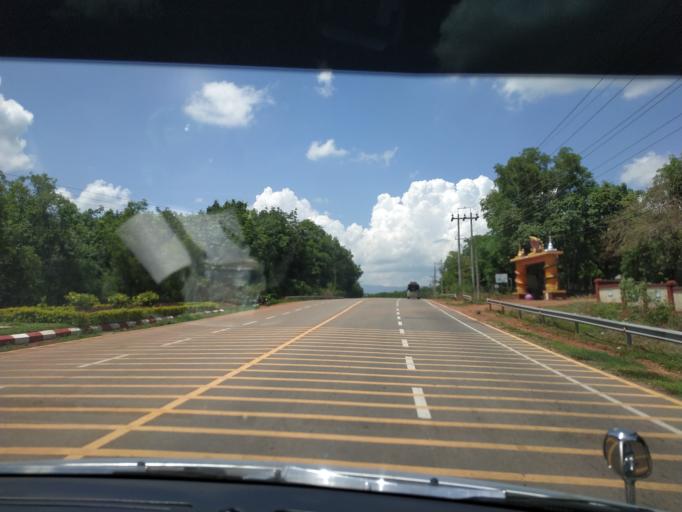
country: MM
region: Mon
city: Kyaikto
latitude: 17.3235
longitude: 97.0224
